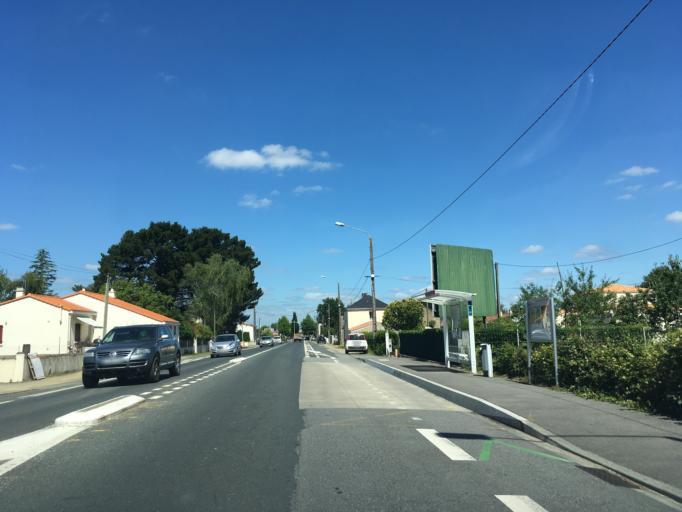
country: FR
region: Pays de la Loire
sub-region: Departement de la Loire-Atlantique
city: Les Sorinieres
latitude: 47.1438
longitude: -1.5256
